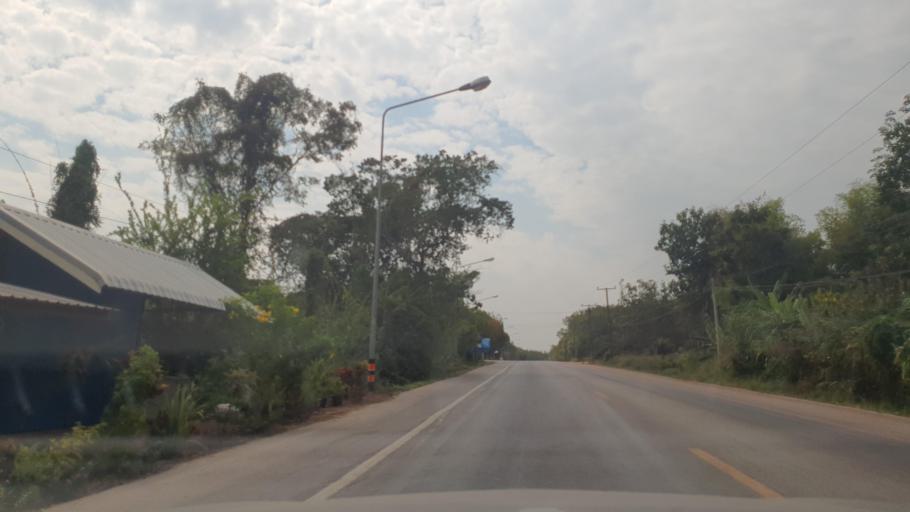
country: TH
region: Changwat Bueng Kan
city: Si Wilai
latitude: 18.2828
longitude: 103.7921
